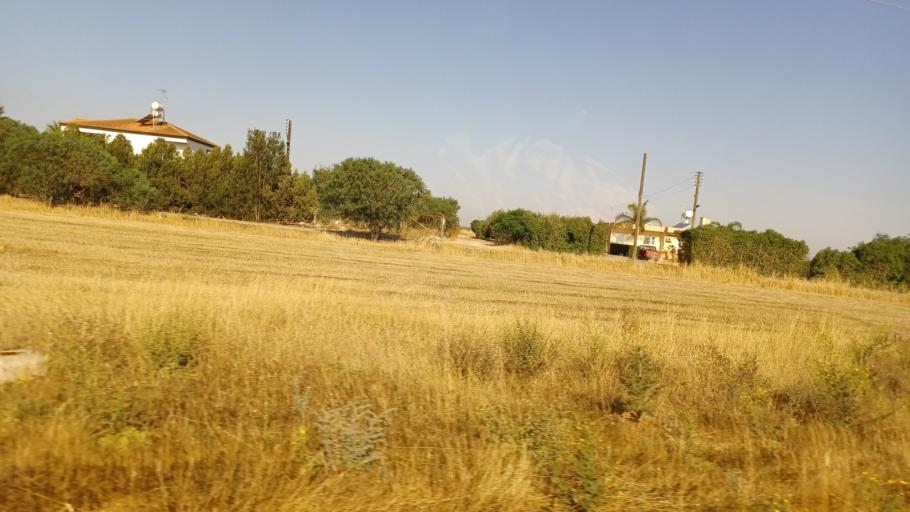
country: CY
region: Ammochostos
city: Frenaros
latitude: 35.0489
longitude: 33.9224
